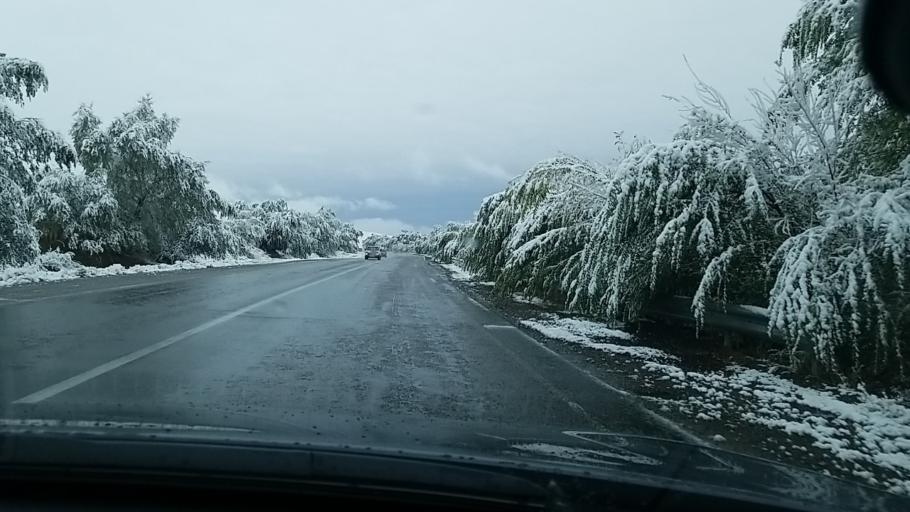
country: KZ
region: Almaty Oblysy
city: Burunday
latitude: 43.2901
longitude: 76.2471
